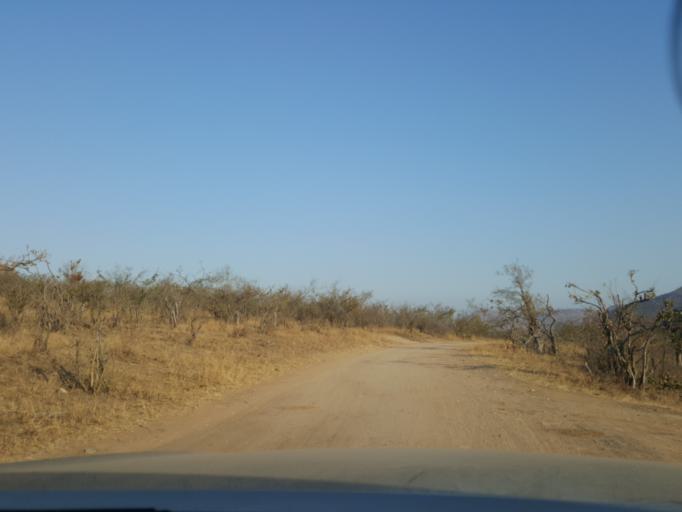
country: ZA
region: Mpumalanga
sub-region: Ehlanzeni District
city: White River
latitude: -25.4026
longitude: 31.4374
